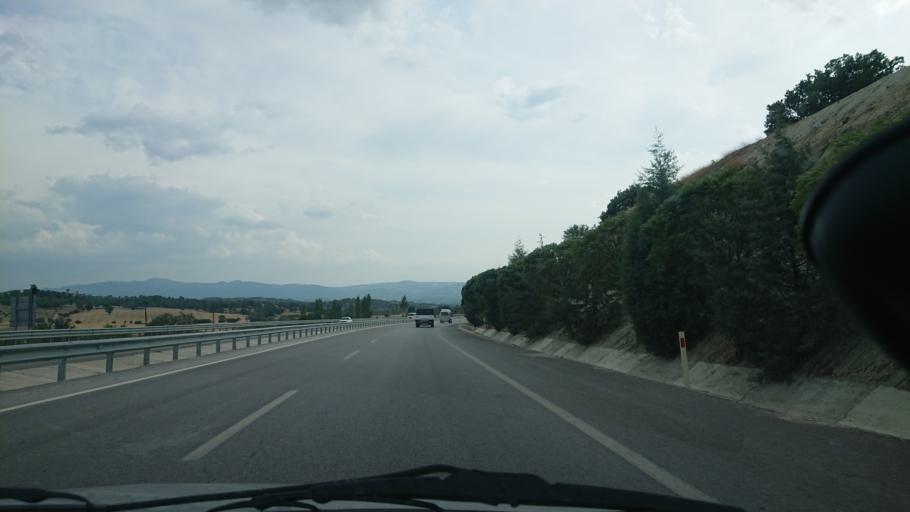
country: TR
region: Kuetahya
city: Gediz
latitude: 39.0201
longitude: 29.4132
